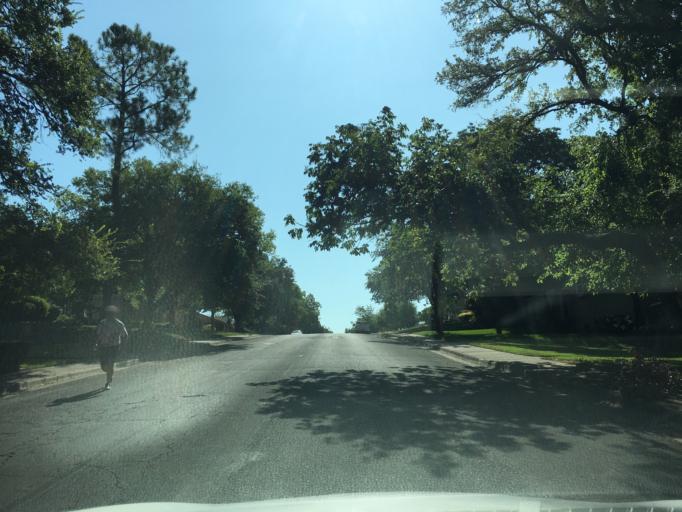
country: US
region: Texas
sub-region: Dallas County
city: Garland
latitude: 32.8576
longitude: -96.6964
